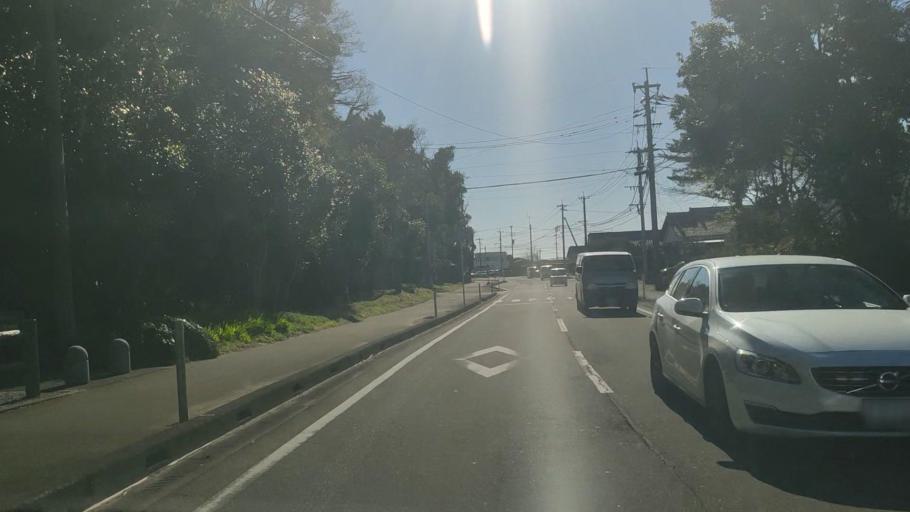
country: JP
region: Miyazaki
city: Miyazaki-shi
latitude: 31.9583
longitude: 131.4638
